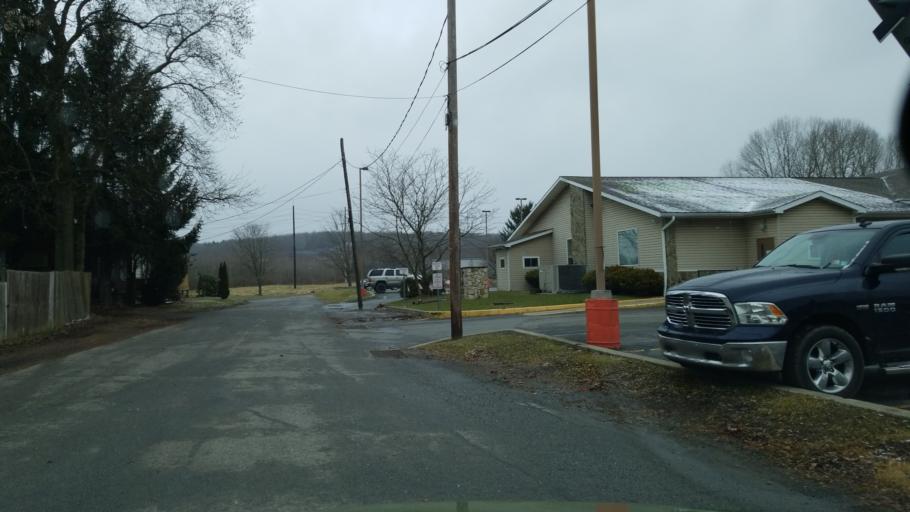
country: US
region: Pennsylvania
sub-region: Clearfield County
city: DuBois
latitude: 41.1246
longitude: -78.7670
